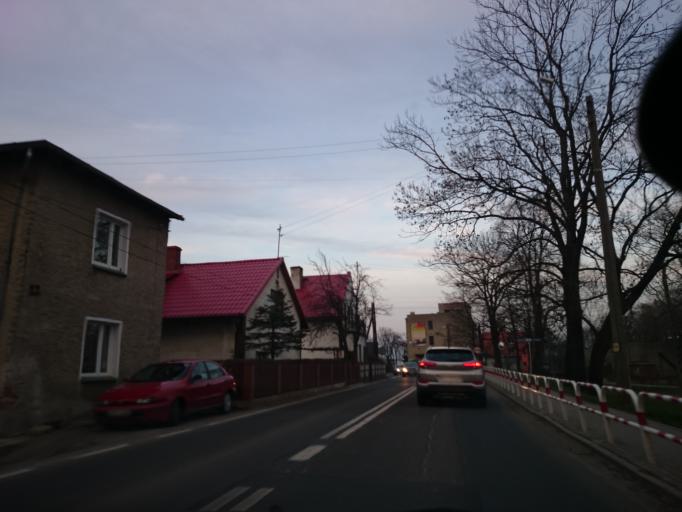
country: PL
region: Opole Voivodeship
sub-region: Powiat prudnicki
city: Laka Prudnicka
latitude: 50.3186
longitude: 17.5406
